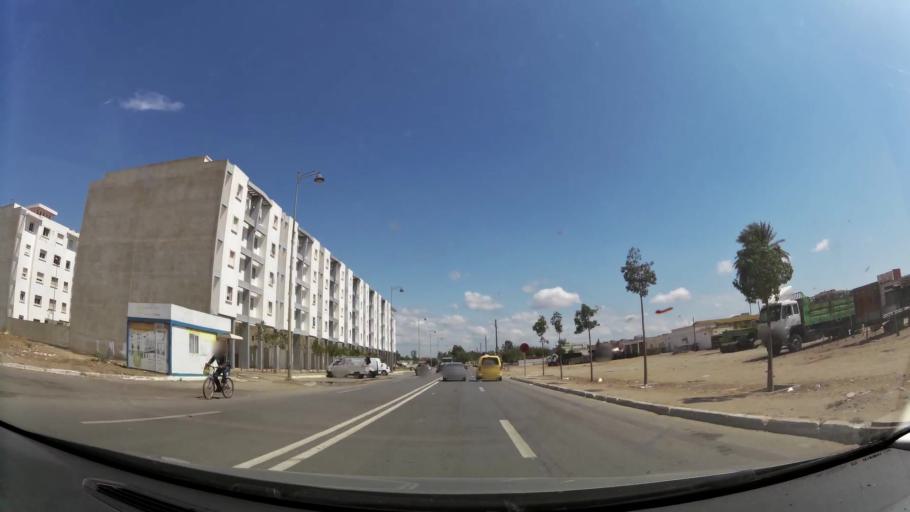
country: MA
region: Gharb-Chrarda-Beni Hssen
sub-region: Kenitra Province
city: Kenitra
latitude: 34.2364
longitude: -6.5440
